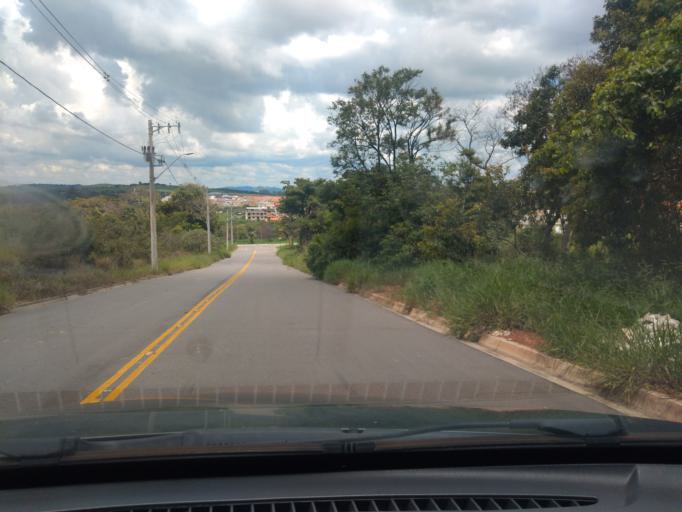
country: BR
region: Minas Gerais
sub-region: Tres Coracoes
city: Tres Coracoes
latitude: -21.6798
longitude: -45.2757
